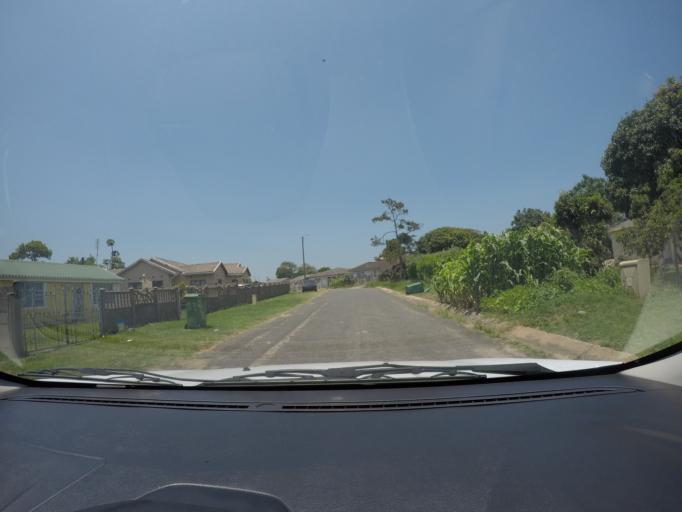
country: ZA
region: KwaZulu-Natal
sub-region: uThungulu District Municipality
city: eSikhawini
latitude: -28.8873
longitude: 31.8879
